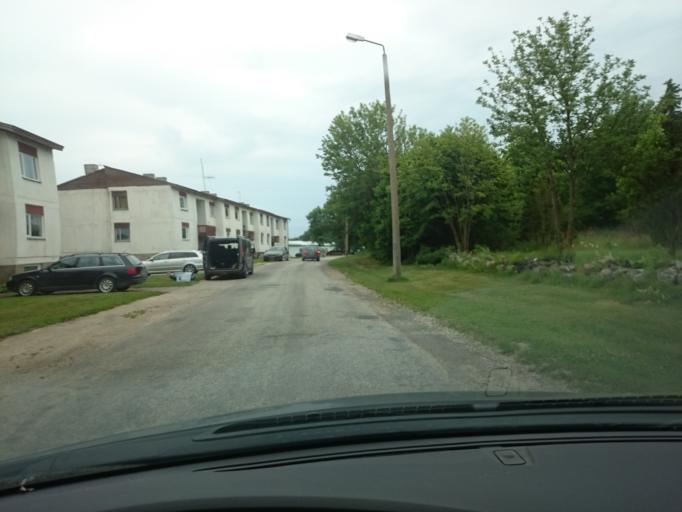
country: EE
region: Saare
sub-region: Orissaare vald
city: Orissaare
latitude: 58.6018
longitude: 23.2317
